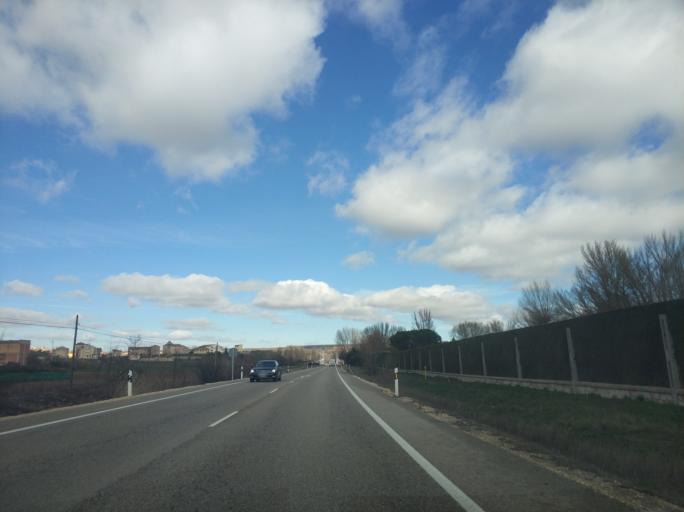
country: ES
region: Castille and Leon
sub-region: Provincia de Burgos
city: Saldana de Burgos
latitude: 42.2561
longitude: -3.6918
